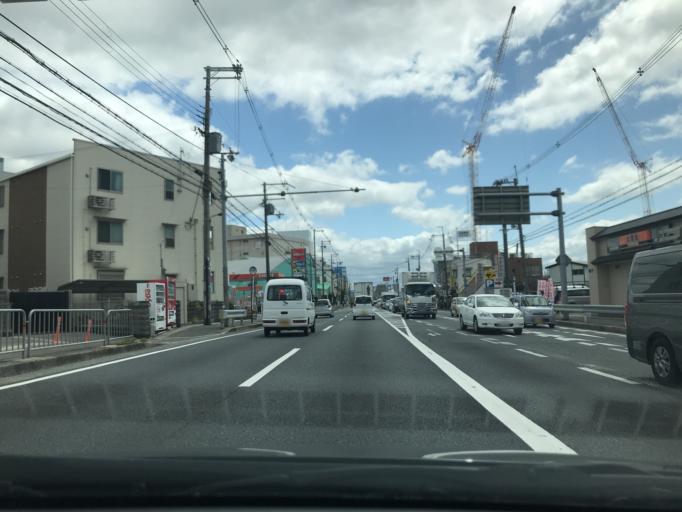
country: JP
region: Osaka
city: Ibaraki
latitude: 34.8360
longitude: 135.5555
